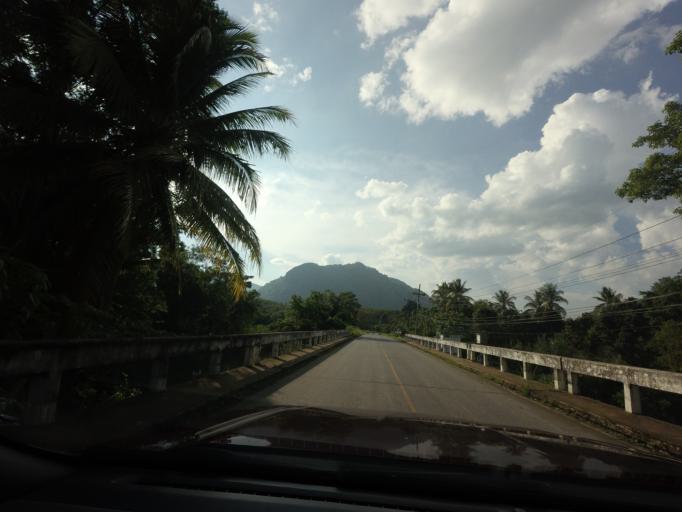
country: TH
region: Yala
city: Ban Nang Sata
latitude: 6.2258
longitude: 101.2225
